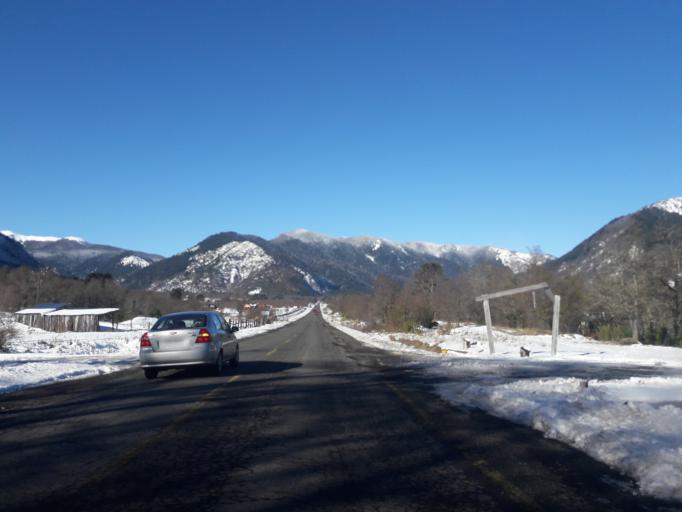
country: CL
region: Araucania
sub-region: Provincia de Cautin
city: Vilcun
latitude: -38.4734
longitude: -71.5583
